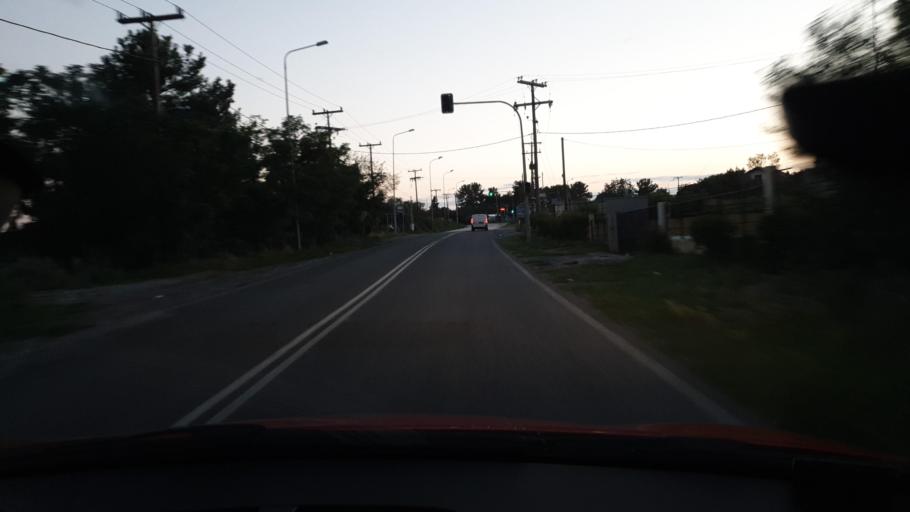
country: GR
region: Central Macedonia
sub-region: Nomos Thessalonikis
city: Agia Triada
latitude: 40.4935
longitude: 22.8710
